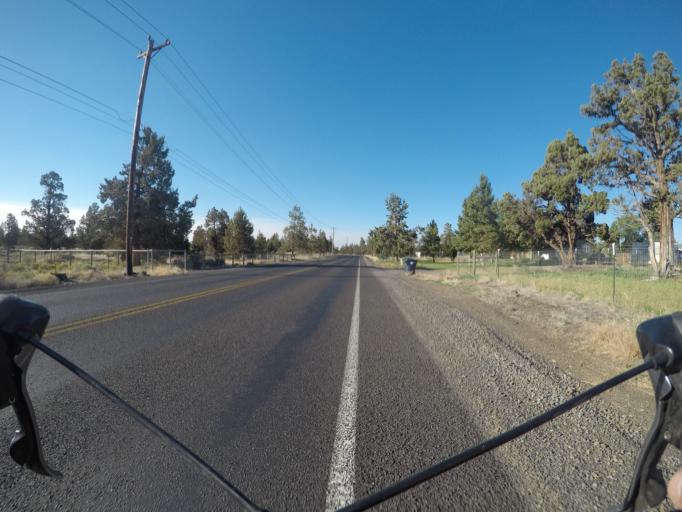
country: US
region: Oregon
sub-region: Deschutes County
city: Redmond
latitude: 44.2260
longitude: -121.2297
